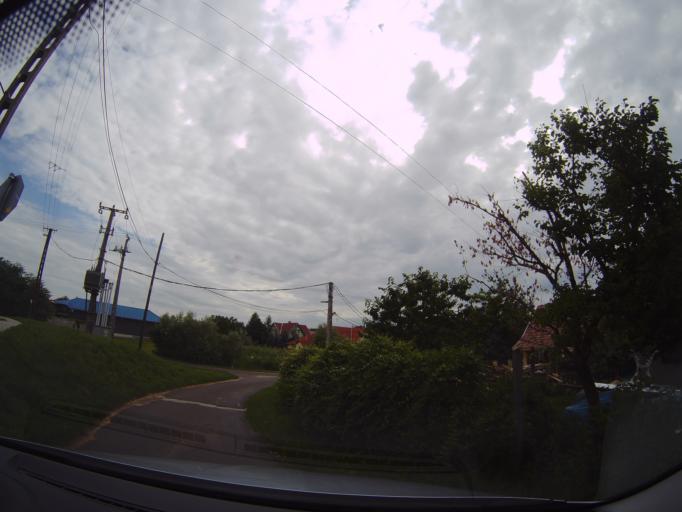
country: HU
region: Pest
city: Orbottyan
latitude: 47.6569
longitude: 19.2358
